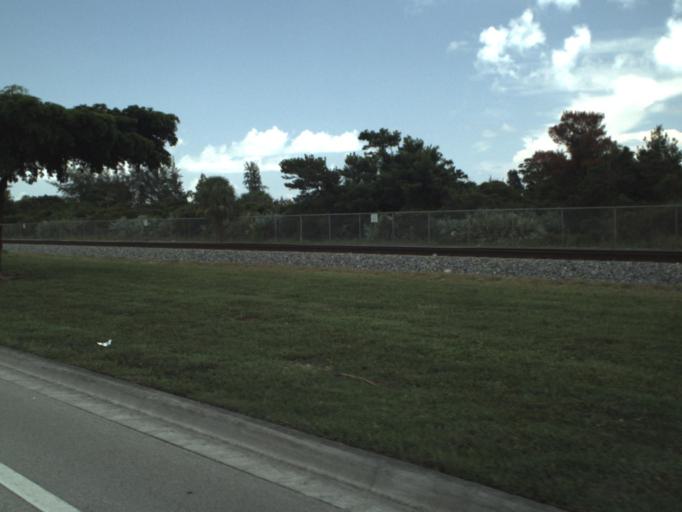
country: US
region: Florida
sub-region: Broward County
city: Pompano Beach Highlands
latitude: 26.2835
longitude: -80.1113
